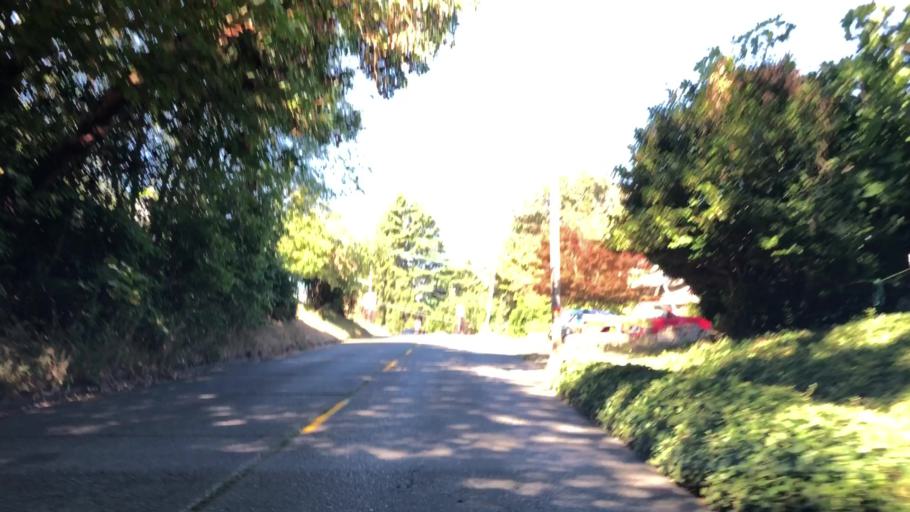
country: US
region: Washington
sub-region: King County
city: Seattle
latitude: 47.6432
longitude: -122.3485
